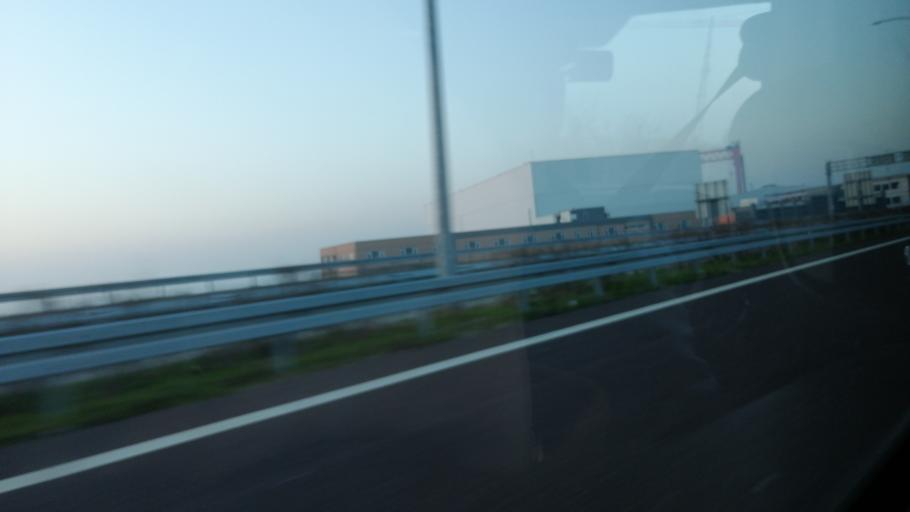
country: TR
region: Yalova
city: Altinova
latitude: 40.7257
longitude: 29.5039
